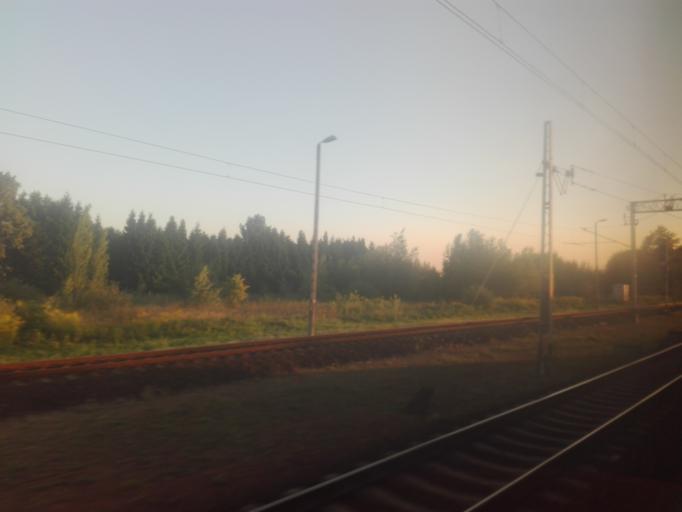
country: PL
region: Masovian Voivodeship
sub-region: Powiat warszawski zachodni
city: Blonie
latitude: 52.1865
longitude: 20.6002
